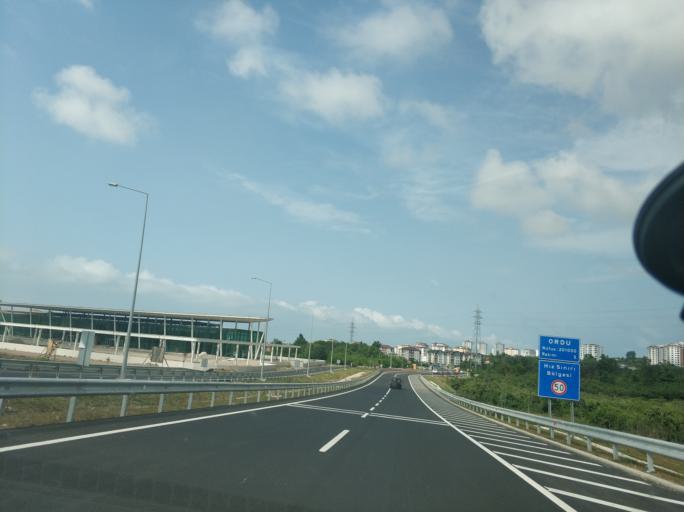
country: TR
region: Ordu
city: Ordu
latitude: 40.9573
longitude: 37.9038
